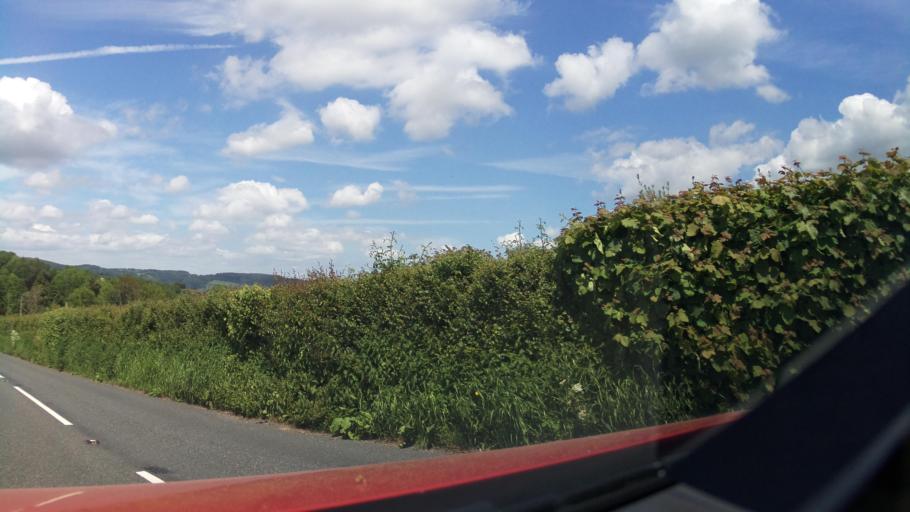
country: GB
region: Wales
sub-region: Monmouthshire
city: Monmouth
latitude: 51.7966
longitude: -2.7181
